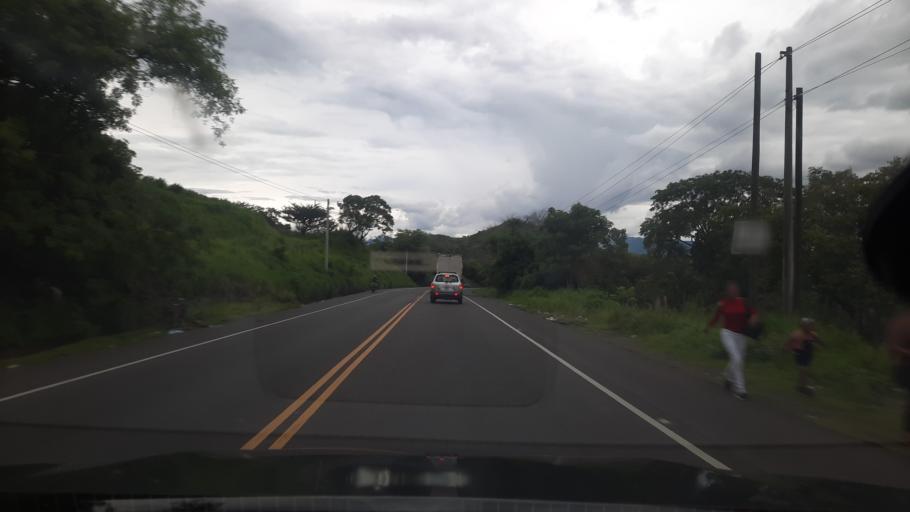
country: HN
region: Choluteca
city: Marcovia
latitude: 13.3540
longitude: -87.2681
